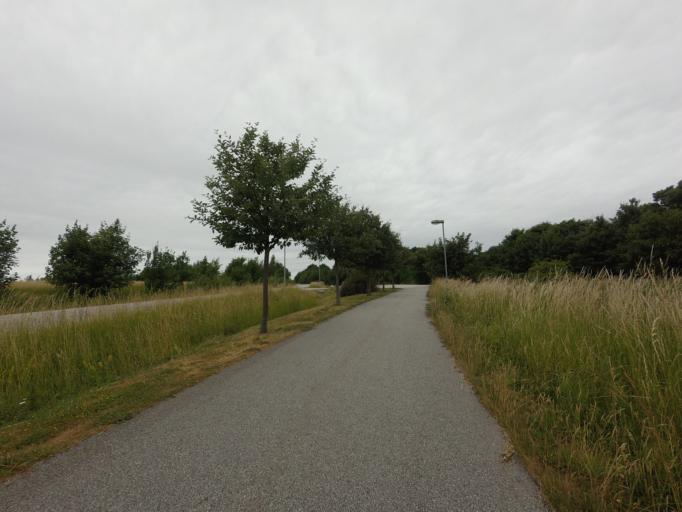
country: SE
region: Skane
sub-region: Malmo
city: Bunkeflostrand
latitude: 55.5682
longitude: 12.9102
